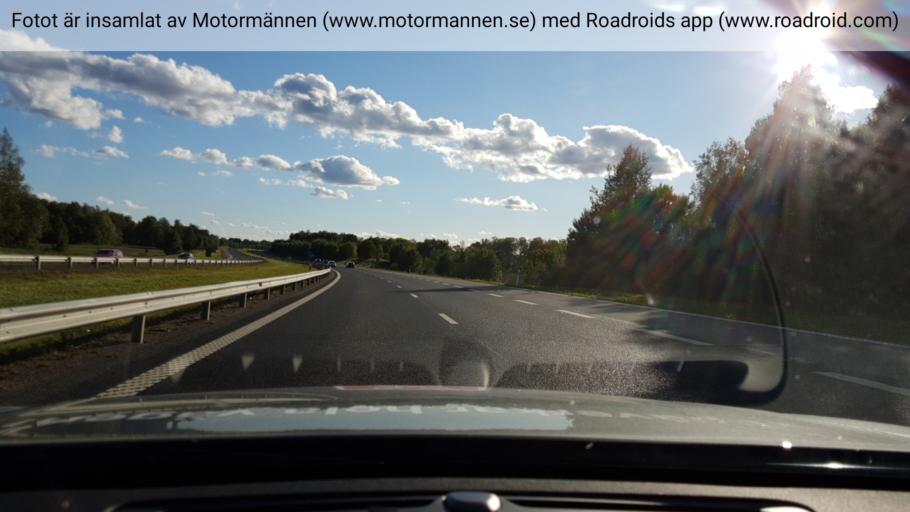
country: SE
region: Vaestmanland
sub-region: Kopings Kommun
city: Koping
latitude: 59.5116
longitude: 15.9430
